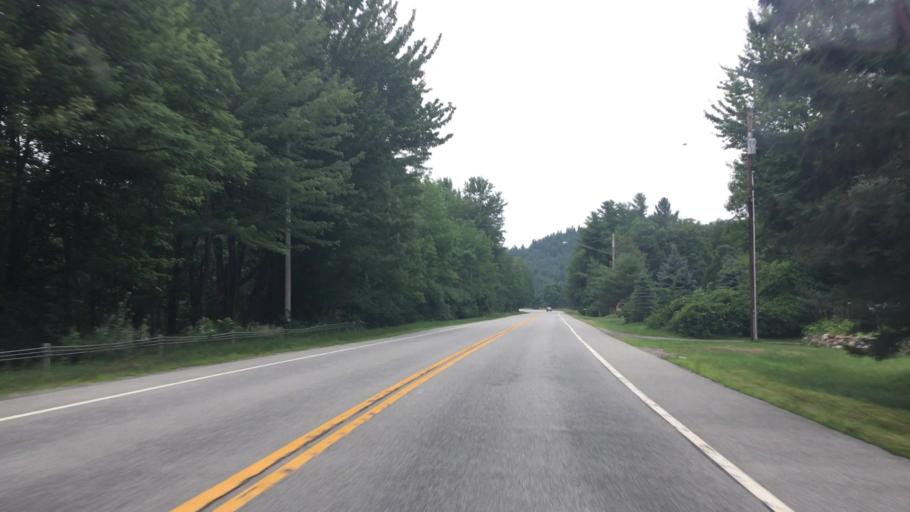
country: US
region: New York
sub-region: Essex County
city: Lake Placid
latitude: 44.3219
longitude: -73.7789
